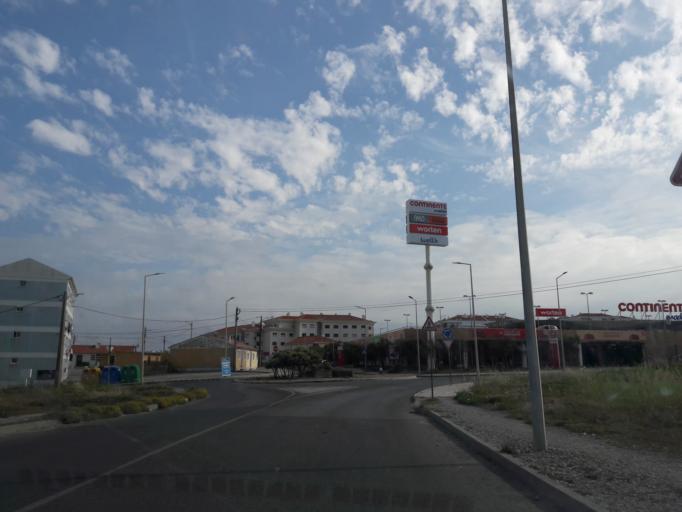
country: PT
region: Leiria
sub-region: Peniche
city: Peniche
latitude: 39.3686
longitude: -9.3830
